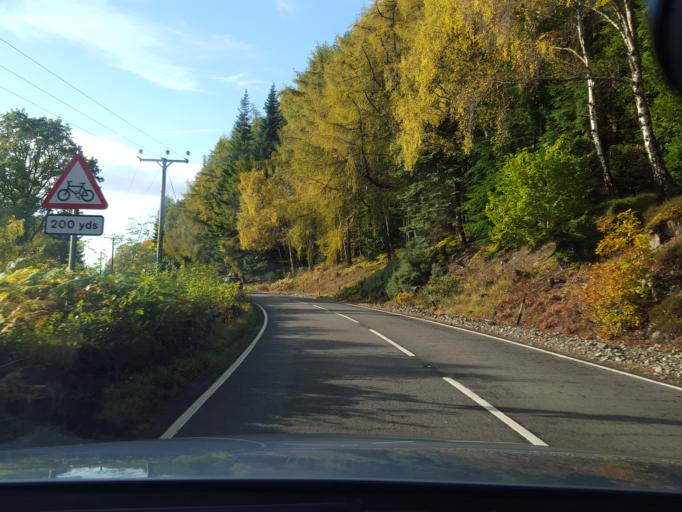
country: GB
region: Scotland
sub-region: Highland
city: Beauly
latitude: 57.2385
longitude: -4.5557
